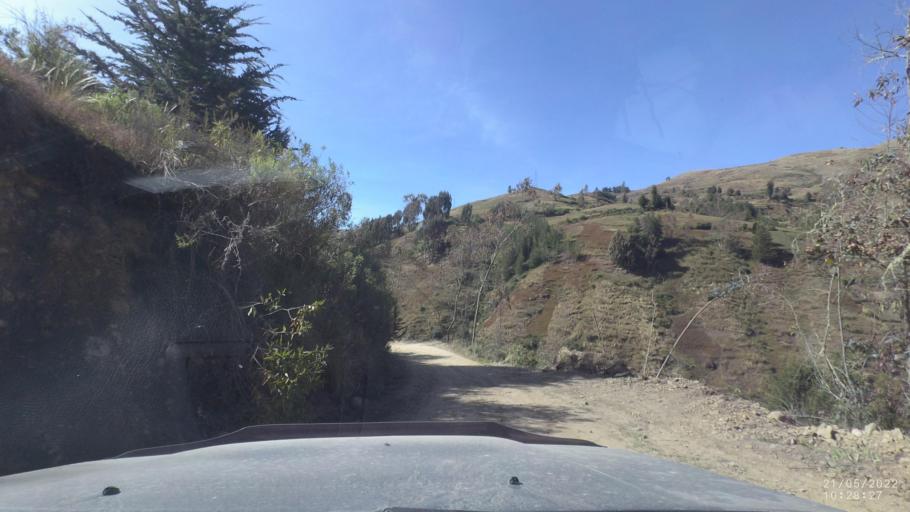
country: BO
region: Cochabamba
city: Colomi
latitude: -17.3218
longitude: -65.9416
